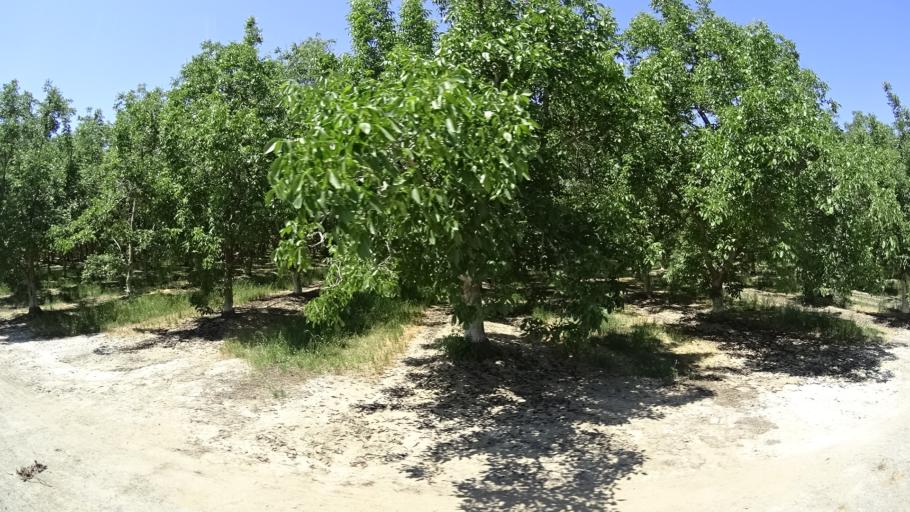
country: US
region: California
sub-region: Kings County
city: Armona
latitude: 36.2502
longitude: -119.6910
